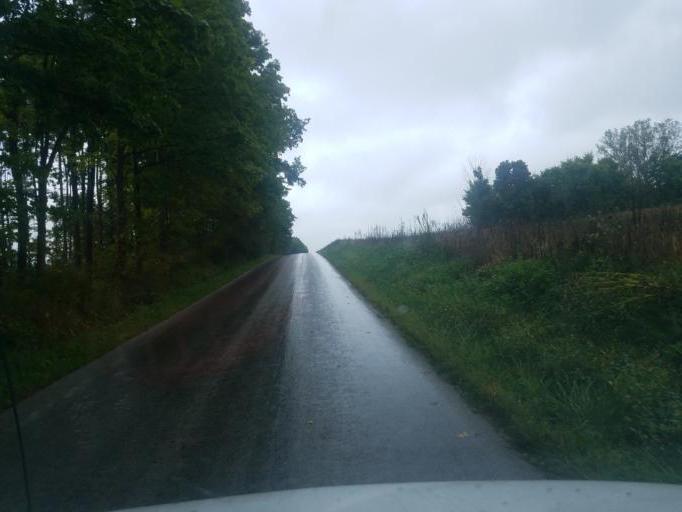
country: US
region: Ohio
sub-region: Wayne County
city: West Salem
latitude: 40.9377
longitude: -82.0450
